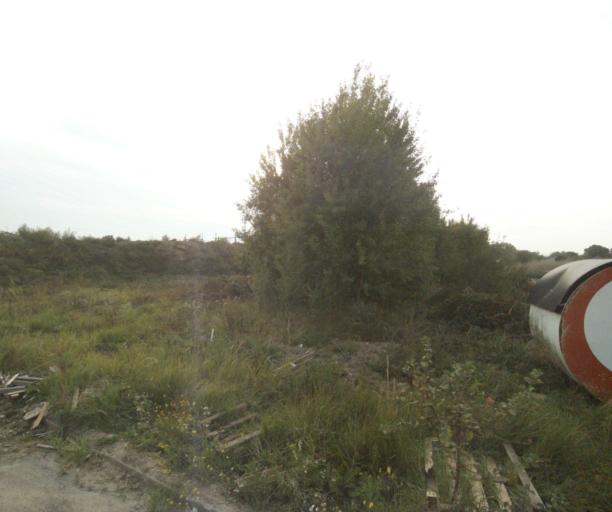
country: FR
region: Nord-Pas-de-Calais
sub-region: Departement du Nord
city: Seclin
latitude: 50.5437
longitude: 3.0481
